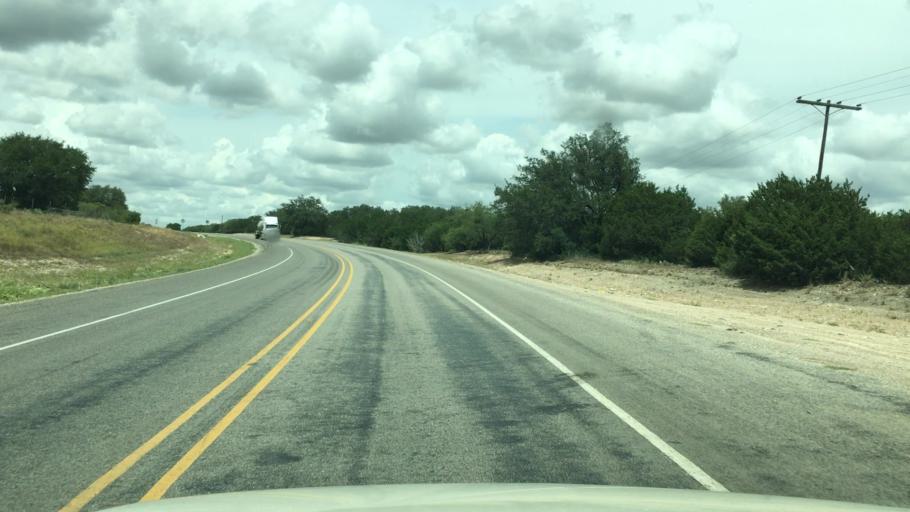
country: US
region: Texas
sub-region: McCulloch County
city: Brady
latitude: 31.0179
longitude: -99.2115
